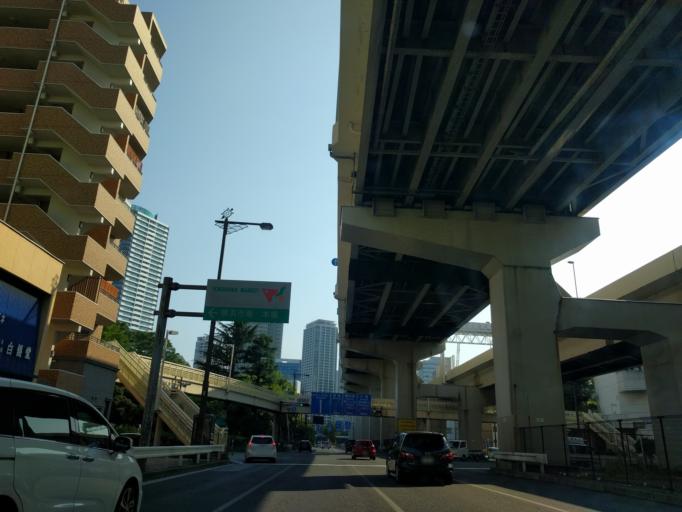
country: JP
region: Kanagawa
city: Yokohama
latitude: 35.4718
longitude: 139.6321
